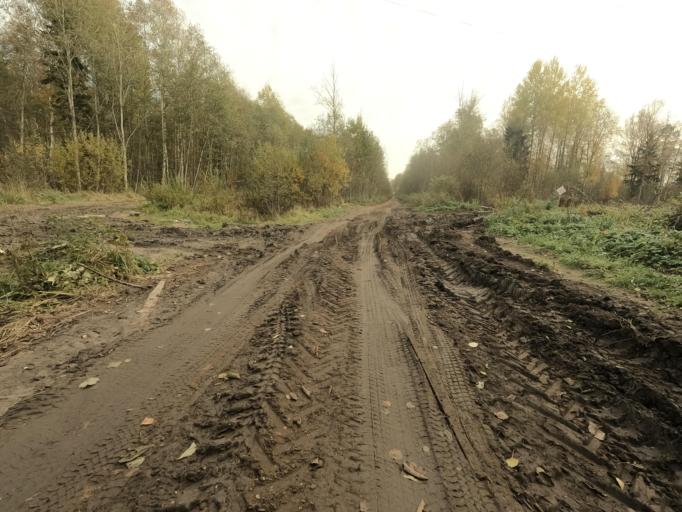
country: RU
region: Novgorod
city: Batetskiy
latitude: 58.8793
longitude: 30.7723
